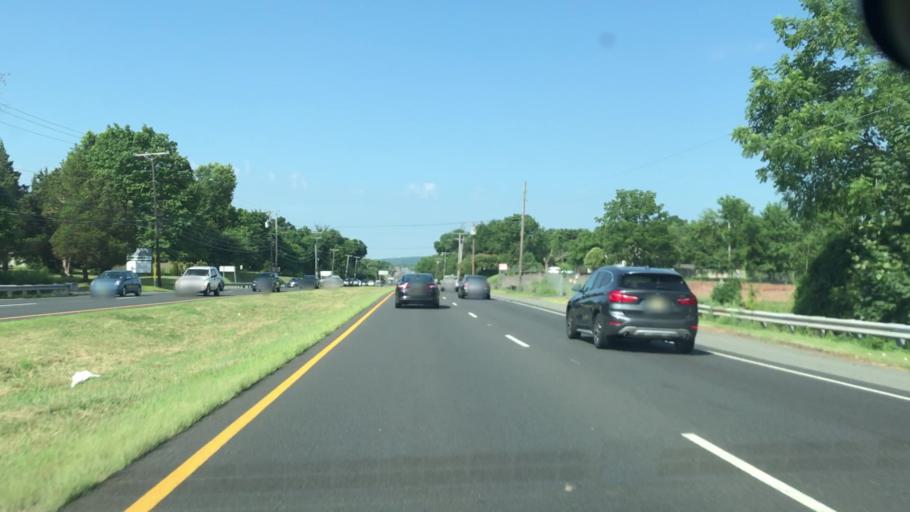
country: US
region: New Jersey
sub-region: Hunterdon County
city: Flemington
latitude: 40.5117
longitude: -74.8313
